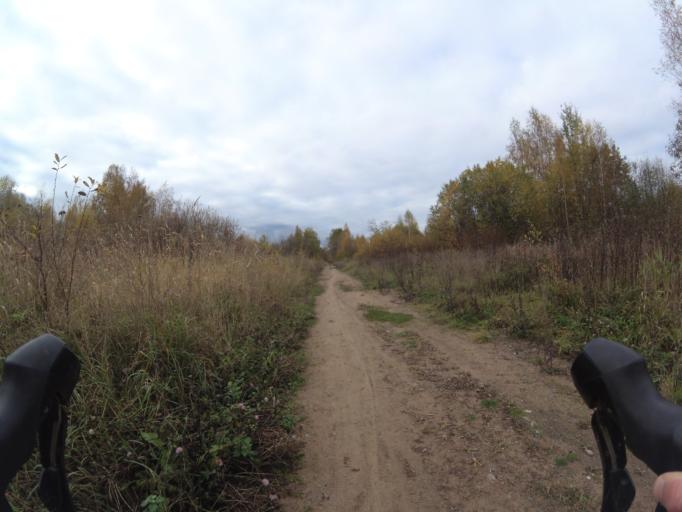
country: RU
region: St.-Petersburg
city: Lakhtinskiy
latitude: 60.0054
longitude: 30.1491
